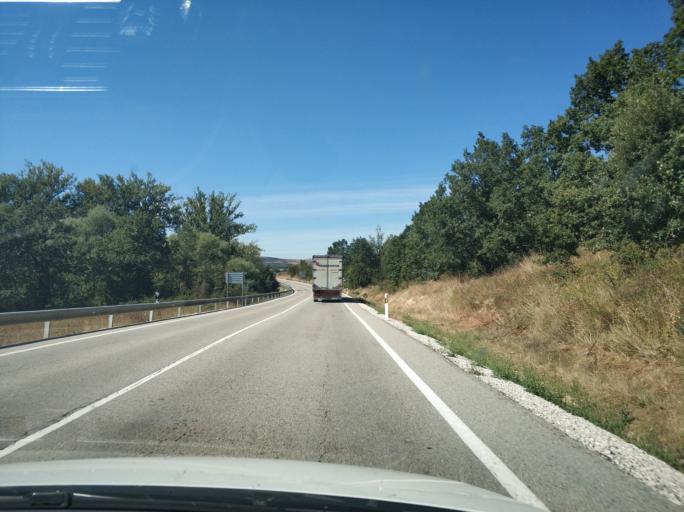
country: ES
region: Castille and Leon
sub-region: Provincia de Burgos
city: Montorio
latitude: 42.6235
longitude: -3.8382
